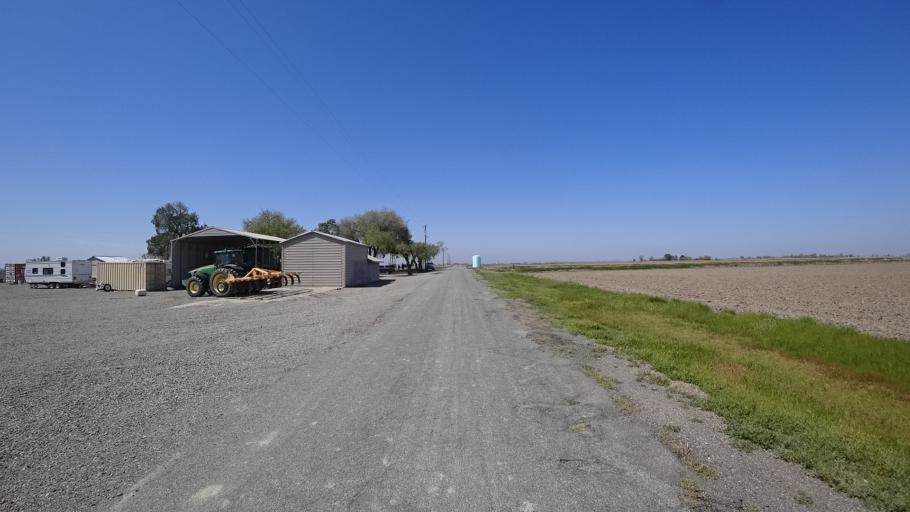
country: US
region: California
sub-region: Glenn County
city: Willows
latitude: 39.4929
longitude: -122.0828
